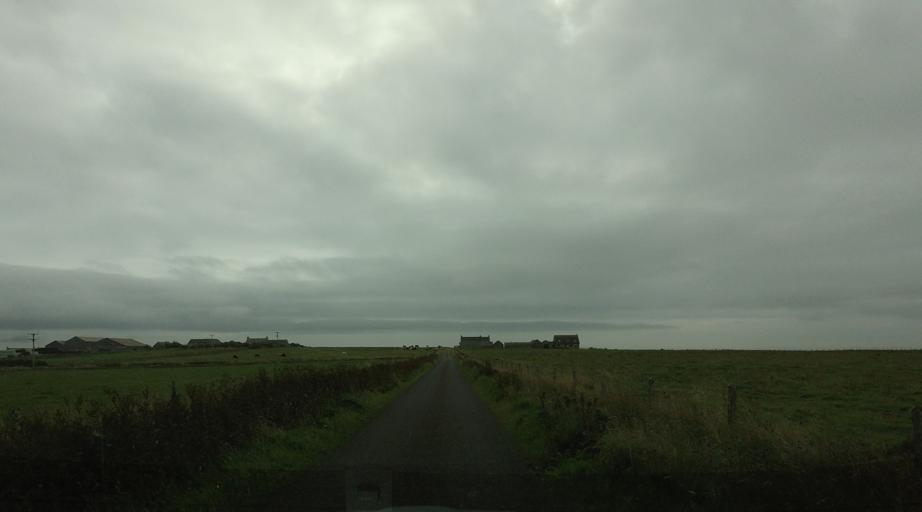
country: GB
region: Scotland
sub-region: Orkney Islands
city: Orkney
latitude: 58.7650
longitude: -2.9622
